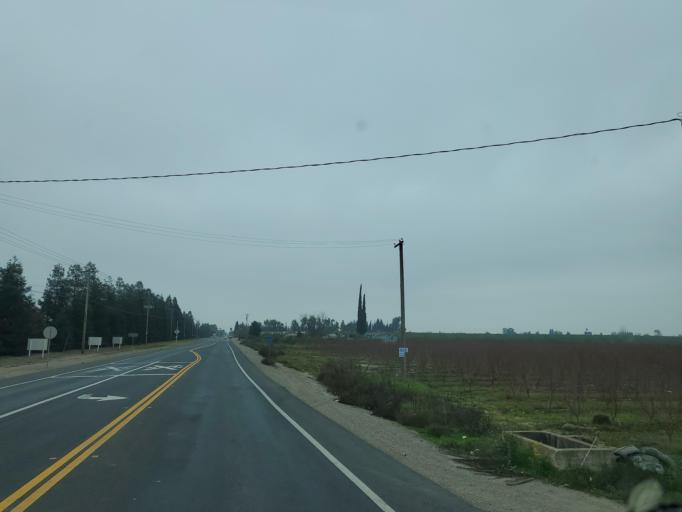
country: US
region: California
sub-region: Stanislaus County
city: Hughson
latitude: 37.5744
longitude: -120.8471
